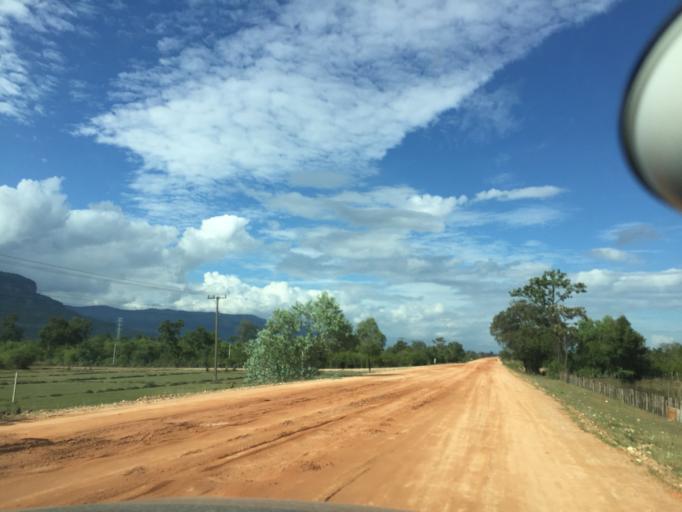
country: LA
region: Attapu
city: Attapu
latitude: 14.6893
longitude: 106.6034
